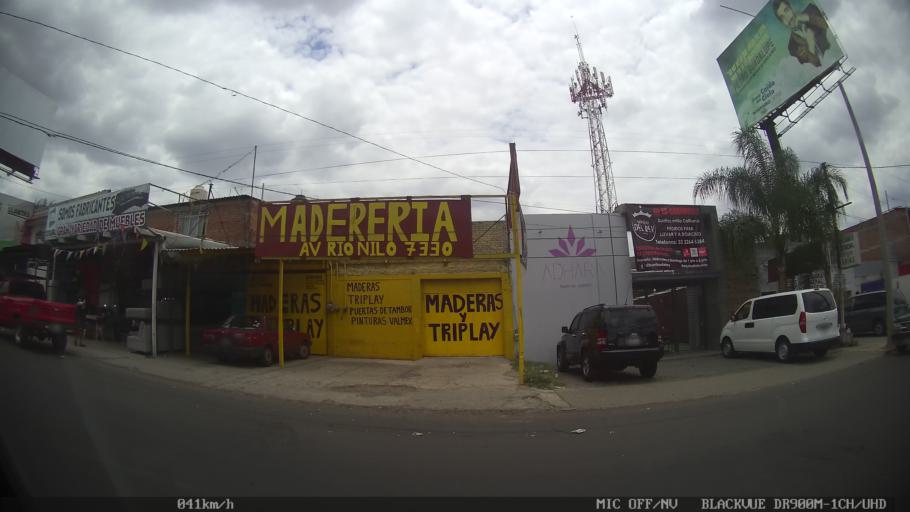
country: MX
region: Jalisco
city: Tlaquepaque
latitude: 20.6387
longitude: -103.2759
